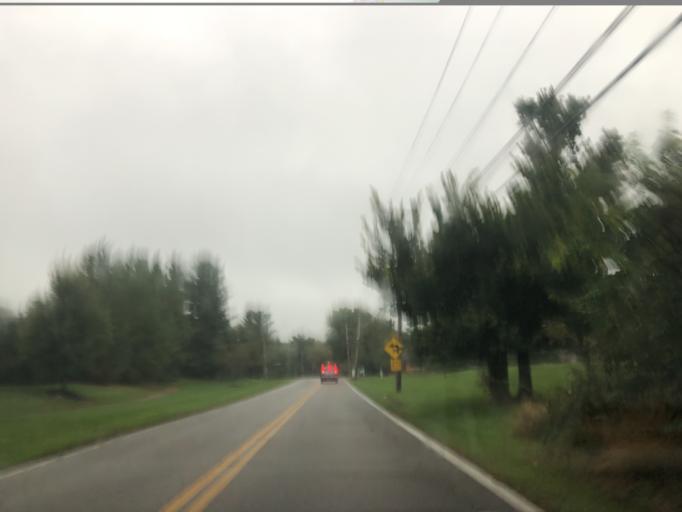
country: US
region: Ohio
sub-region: Clermont County
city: Mulberry
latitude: 39.1971
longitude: -84.2483
